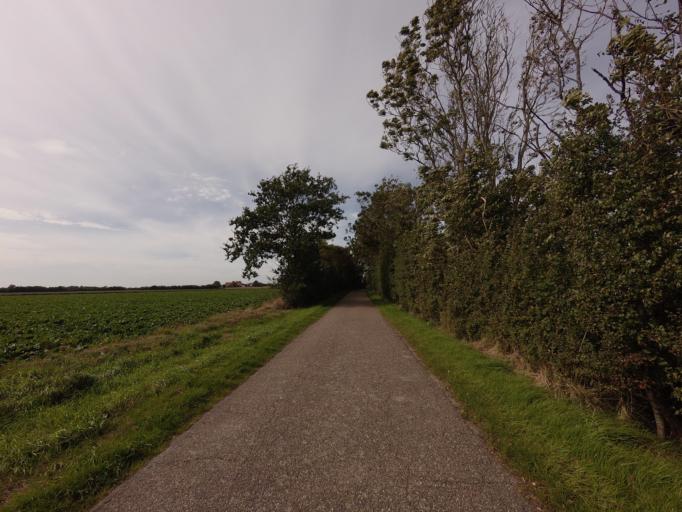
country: NL
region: North Holland
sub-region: Gemeente Texel
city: Den Burg
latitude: 53.0716
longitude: 4.8134
